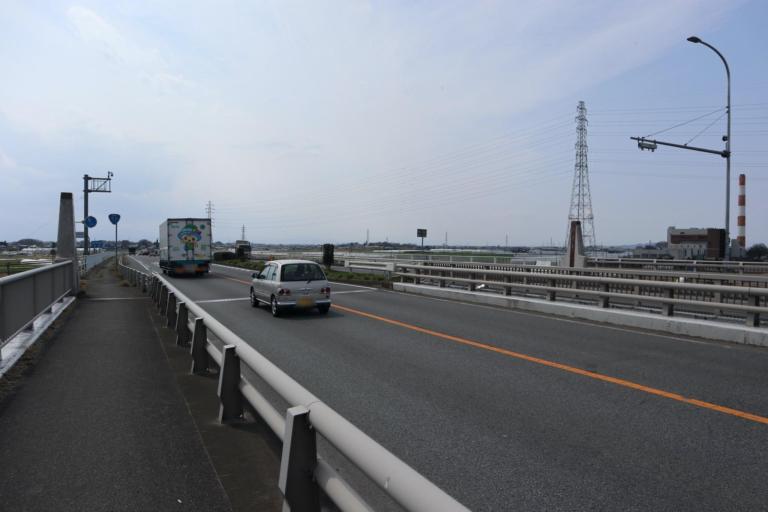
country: JP
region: Gunma
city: Tatebayashi
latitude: 36.2888
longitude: 139.5244
